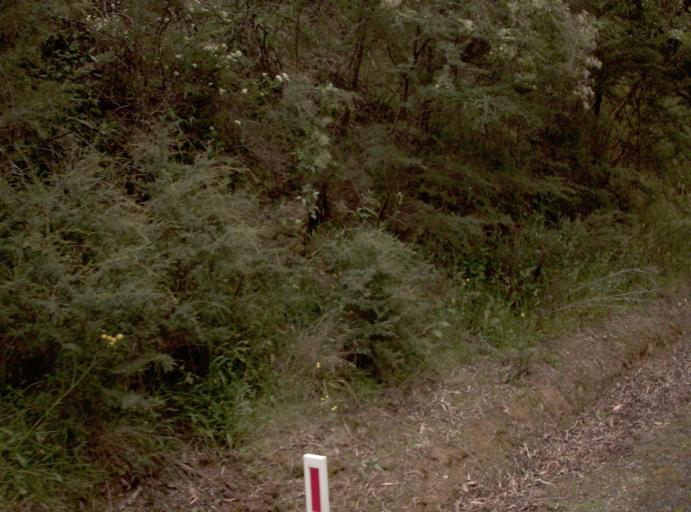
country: AU
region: New South Wales
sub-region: Bombala
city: Bombala
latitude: -37.3824
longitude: 149.2013
